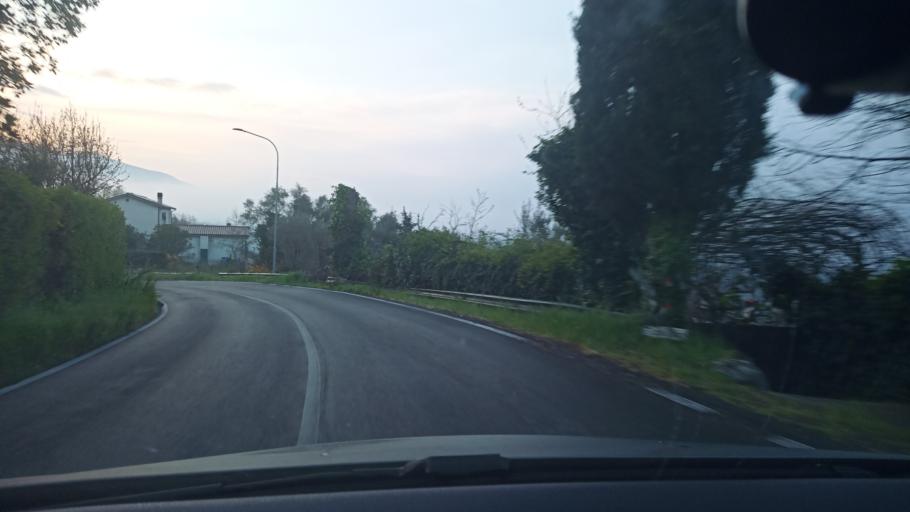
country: IT
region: Latium
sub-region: Provincia di Rieti
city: Cantalupo in Sabina
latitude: 42.2981
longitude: 12.6478
